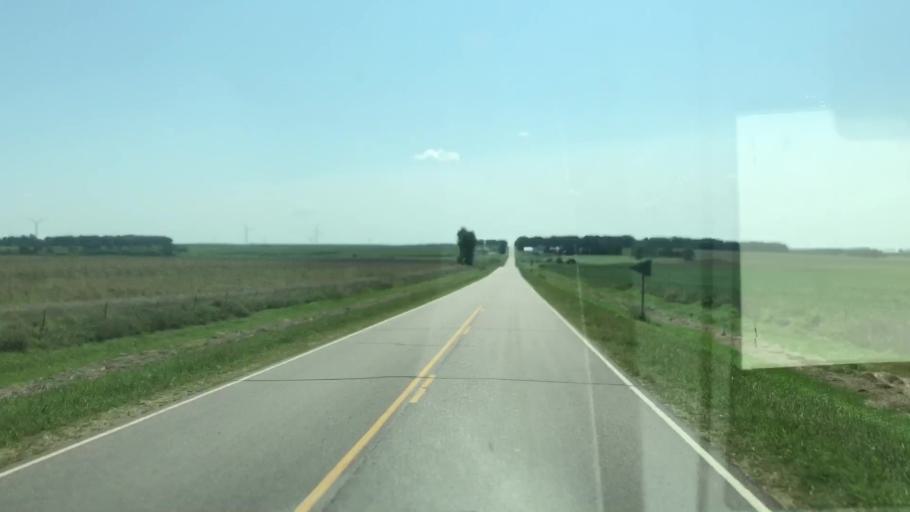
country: US
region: Iowa
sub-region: O'Brien County
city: Sanborn
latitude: 43.2477
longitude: -95.7235
